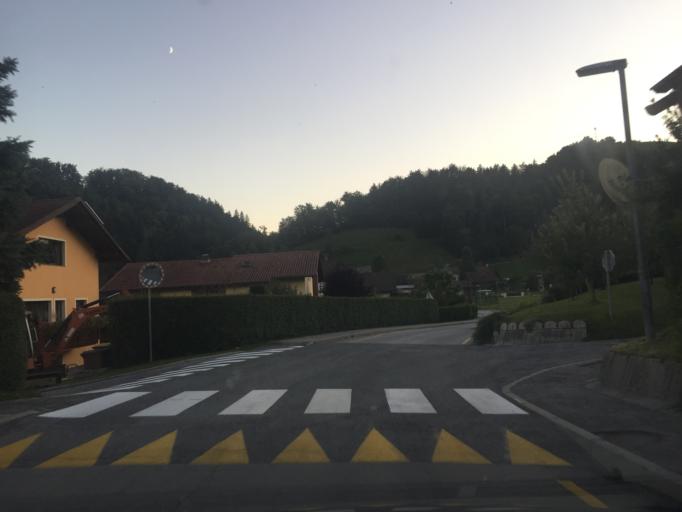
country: SI
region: Sostanj
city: Sostanj
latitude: 46.3835
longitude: 15.0309
